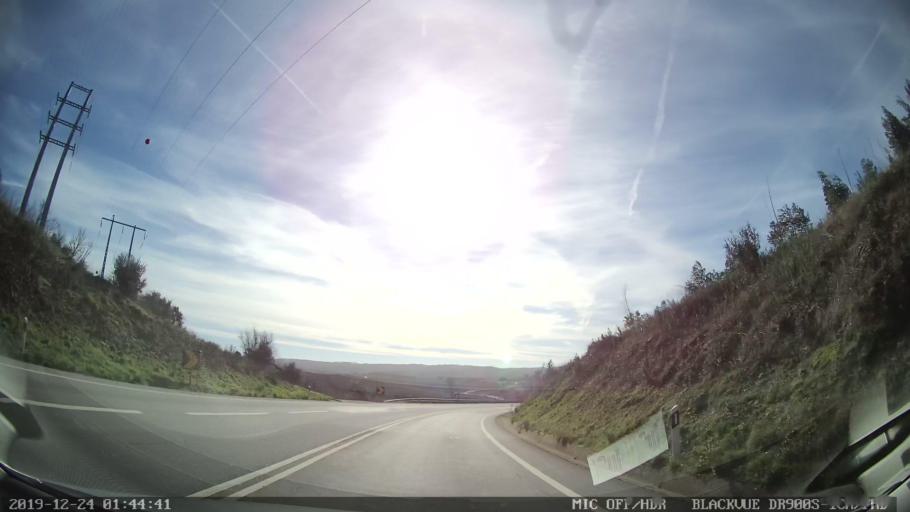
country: PT
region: Portalegre
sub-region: Nisa
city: Nisa
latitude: 39.5516
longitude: -7.7937
